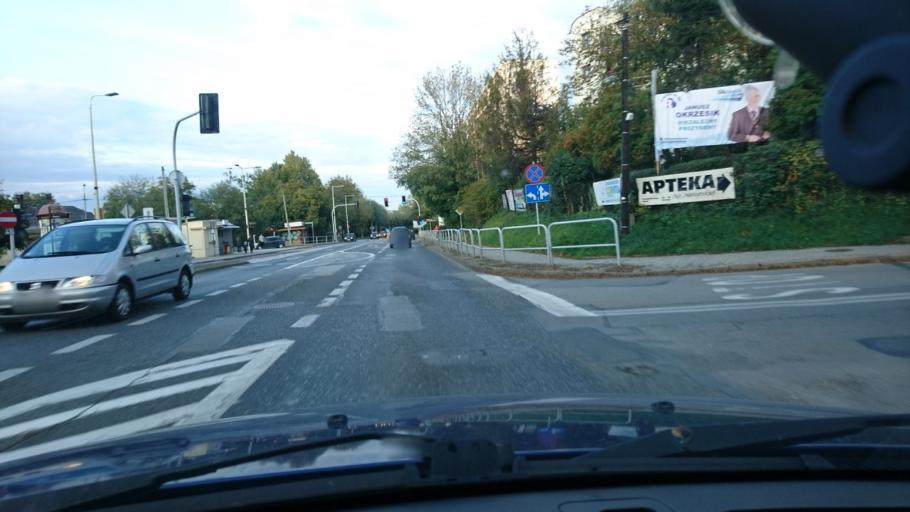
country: PL
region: Silesian Voivodeship
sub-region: Bielsko-Biala
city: Bielsko-Biala
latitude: 49.8212
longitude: 19.0236
